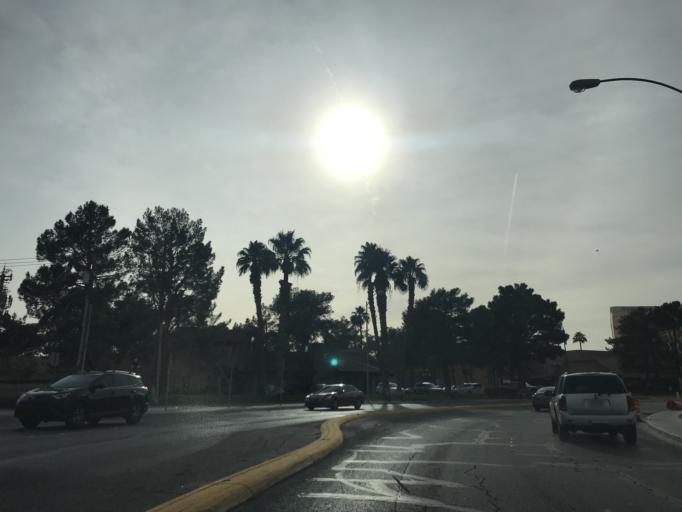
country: US
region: Nevada
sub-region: Clark County
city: Paradise
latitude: 36.0976
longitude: -115.1640
